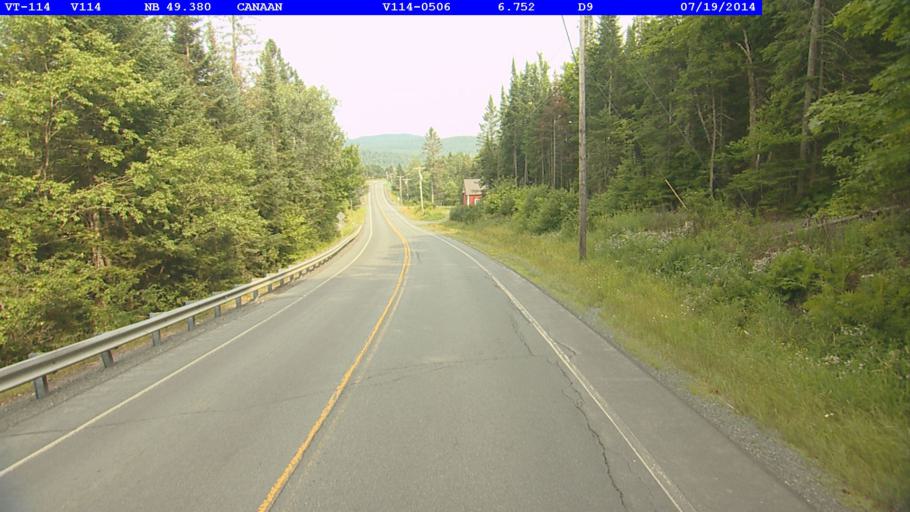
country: US
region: New Hampshire
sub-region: Coos County
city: Colebrook
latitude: 45.0082
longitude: -71.5613
